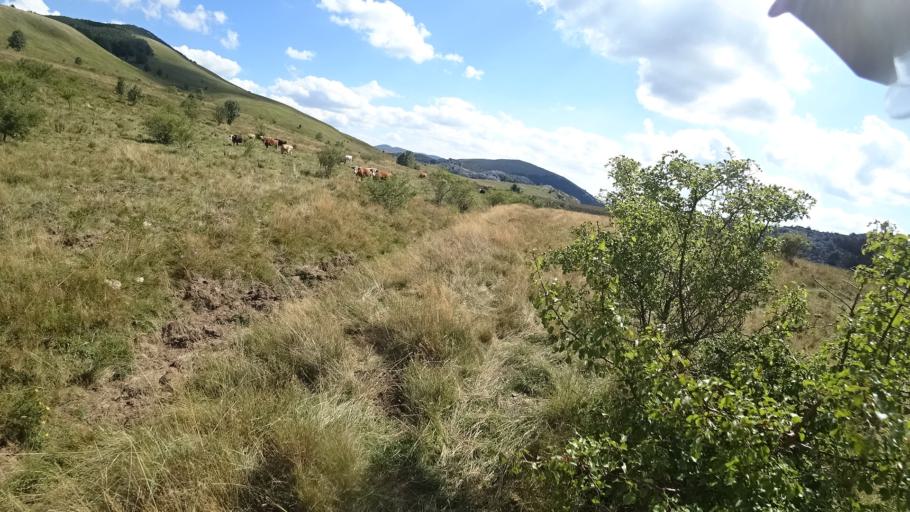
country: HR
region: Zadarska
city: Gracac
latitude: 44.4153
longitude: 16.0016
